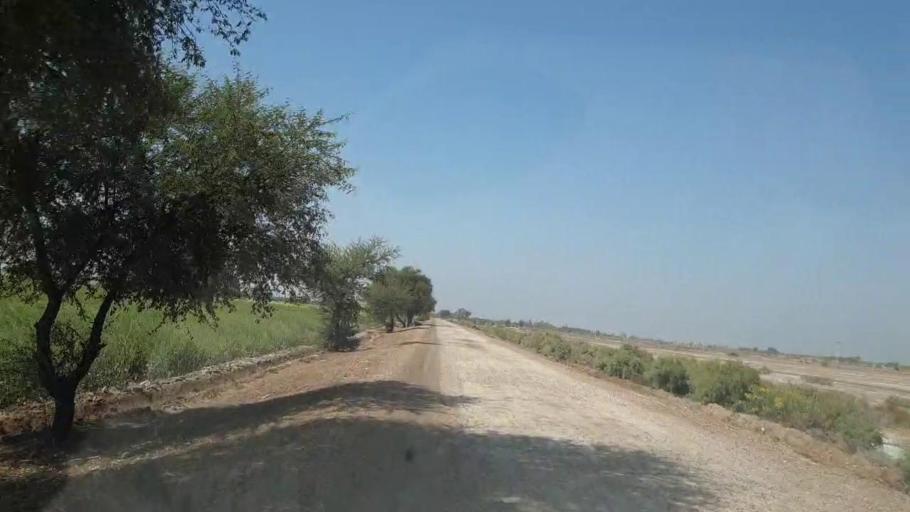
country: PK
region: Sindh
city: Mirpur Khas
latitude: 25.6943
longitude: 69.1080
